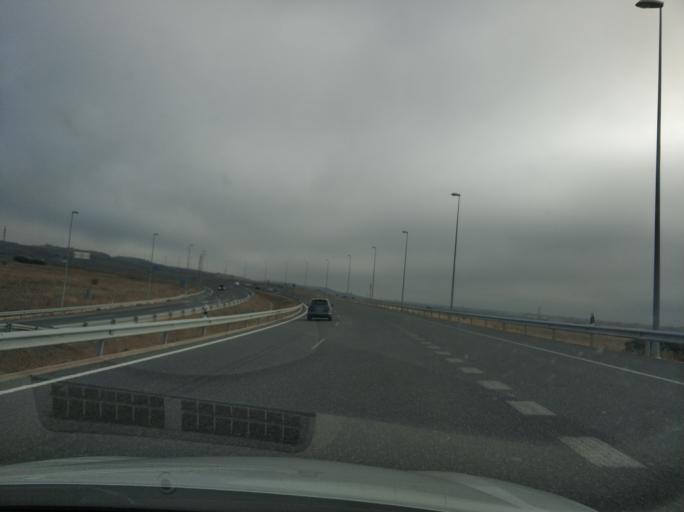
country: ES
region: Castille and Leon
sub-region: Provincia de Leon
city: Leon
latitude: 42.5679
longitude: -5.5447
